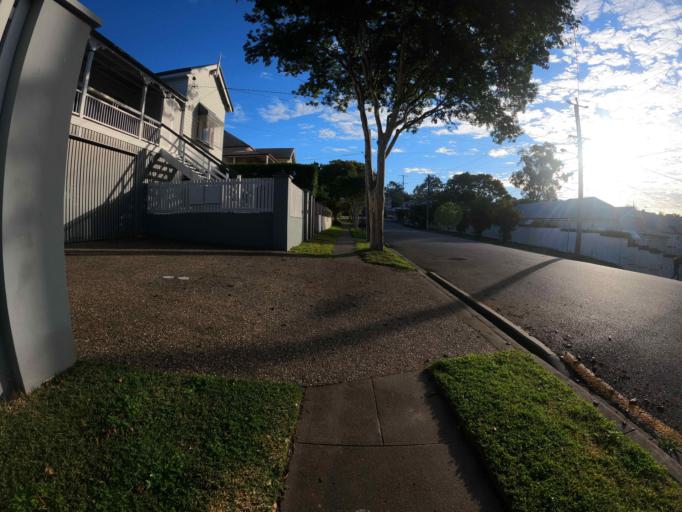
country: AU
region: Queensland
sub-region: Brisbane
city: Windsor
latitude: -27.4386
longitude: 153.0279
